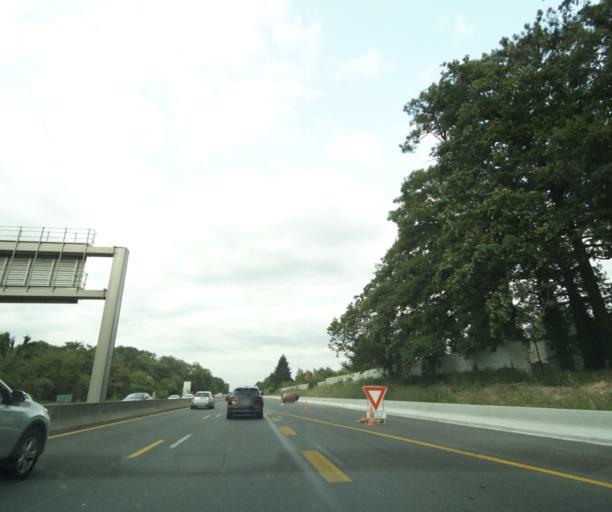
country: FR
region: Centre
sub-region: Departement d'Indre-et-Loire
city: Chambray-les-Tours
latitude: 47.3537
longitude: 0.7069
